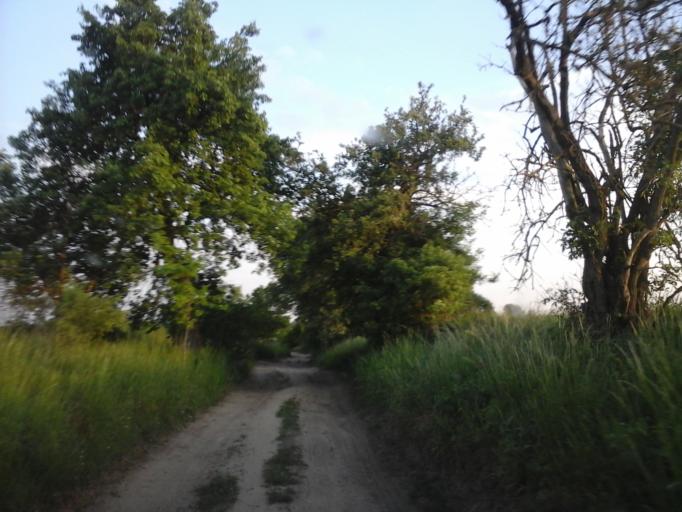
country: PL
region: West Pomeranian Voivodeship
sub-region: Powiat choszczenski
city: Choszczno
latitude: 53.1917
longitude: 15.4172
